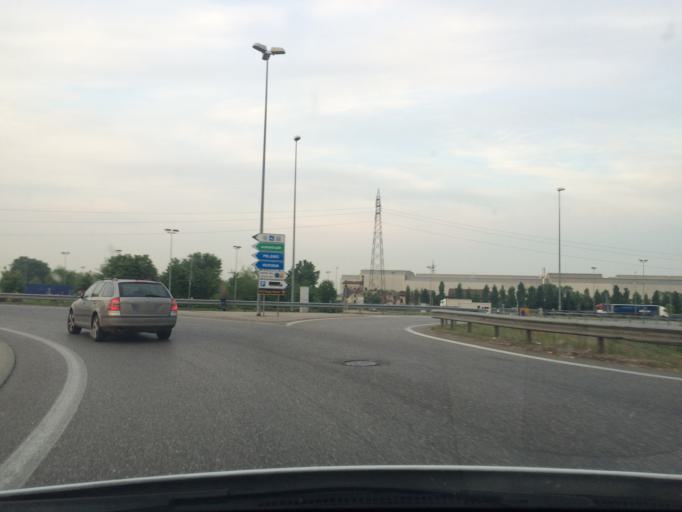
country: IT
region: Lombardy
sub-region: Provincia di Brescia
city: San Zeno Naviglio
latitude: 45.5086
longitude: 10.2290
